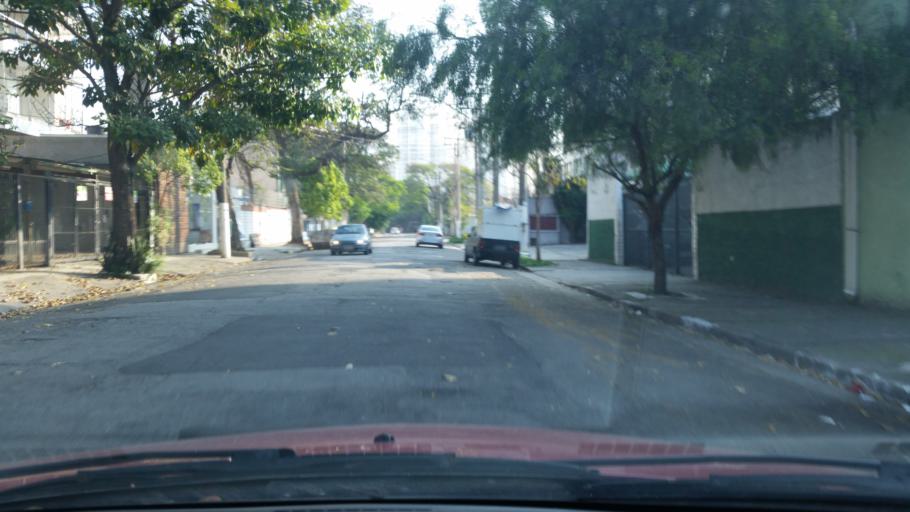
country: BR
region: Sao Paulo
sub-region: Osasco
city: Osasco
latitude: -23.5243
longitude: -46.7344
